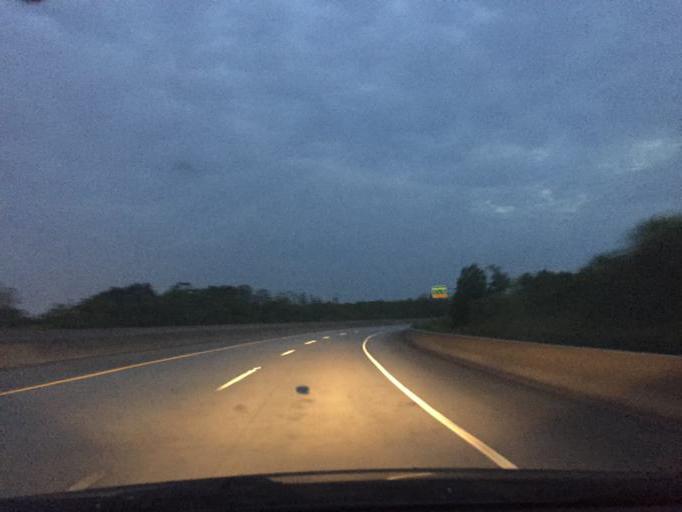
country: US
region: Georgia
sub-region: Chatham County
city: Savannah
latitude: 32.0655
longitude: -81.0759
